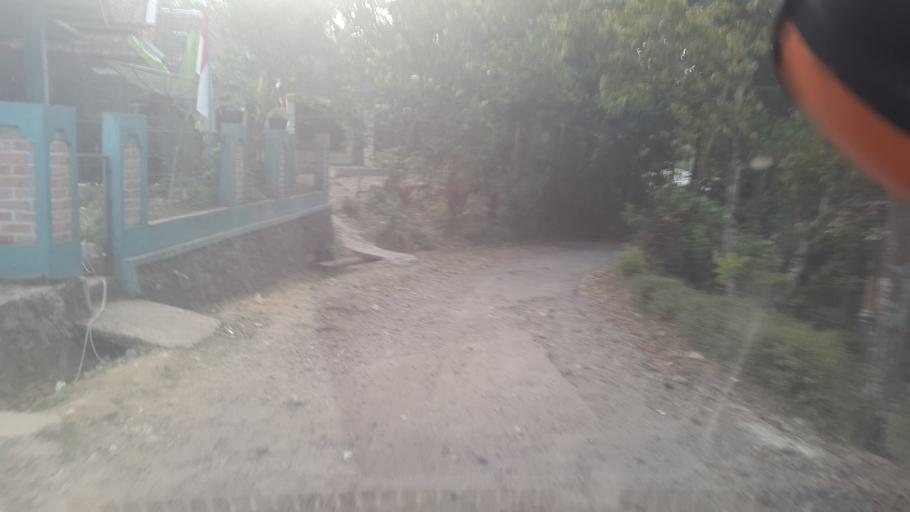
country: ID
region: West Java
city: Sukamaju
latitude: -7.0056
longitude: 106.9018
